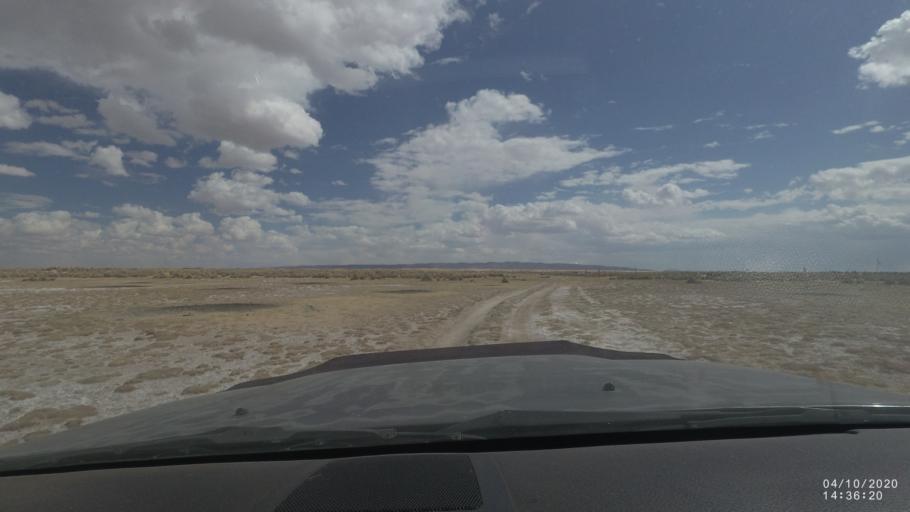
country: BO
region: Oruro
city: Poopo
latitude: -18.6726
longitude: -67.4701
